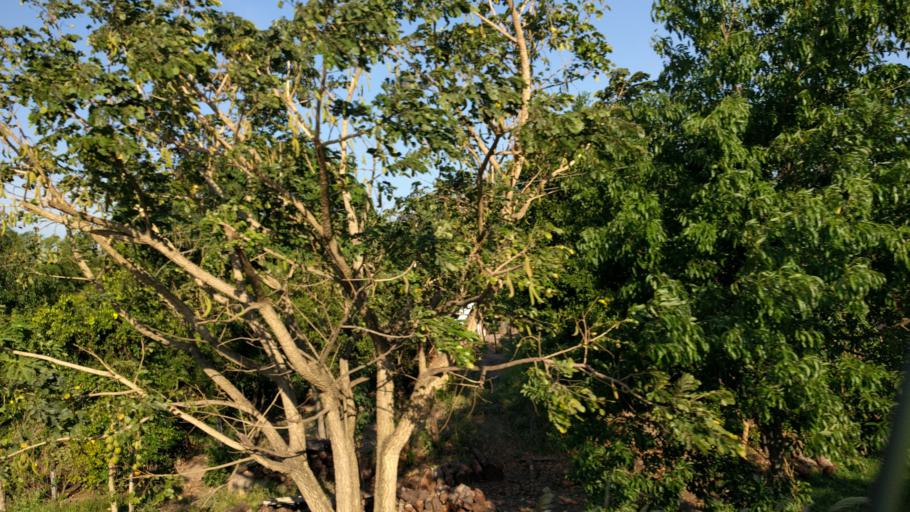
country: BO
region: Santa Cruz
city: Jorochito
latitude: -18.1099
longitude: -63.4581
